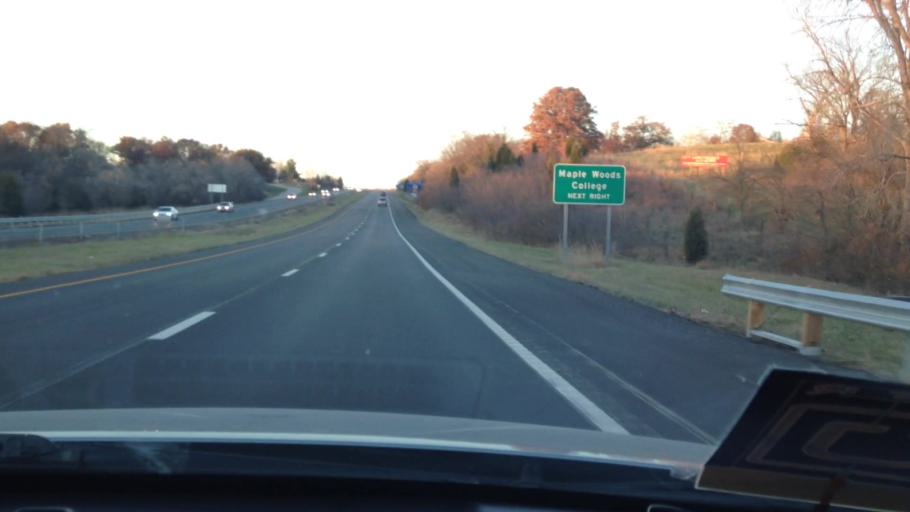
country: US
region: Missouri
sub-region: Clay County
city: Gladstone
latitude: 39.2339
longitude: -94.5895
